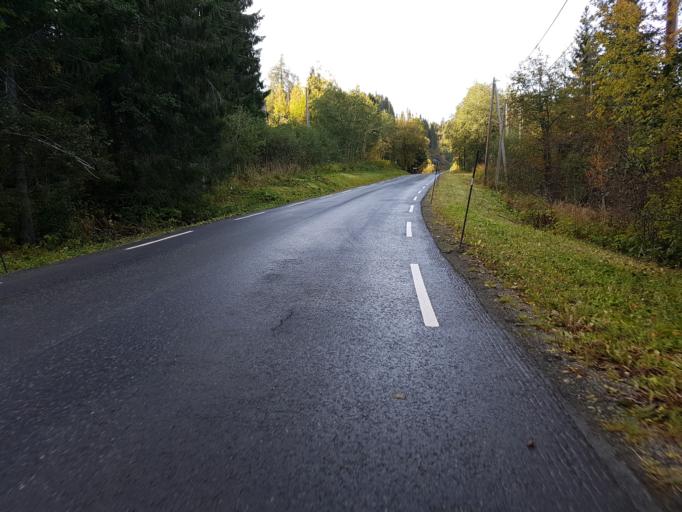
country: NO
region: Sor-Trondelag
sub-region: Klaebu
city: Klaebu
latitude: 63.3443
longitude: 10.5470
